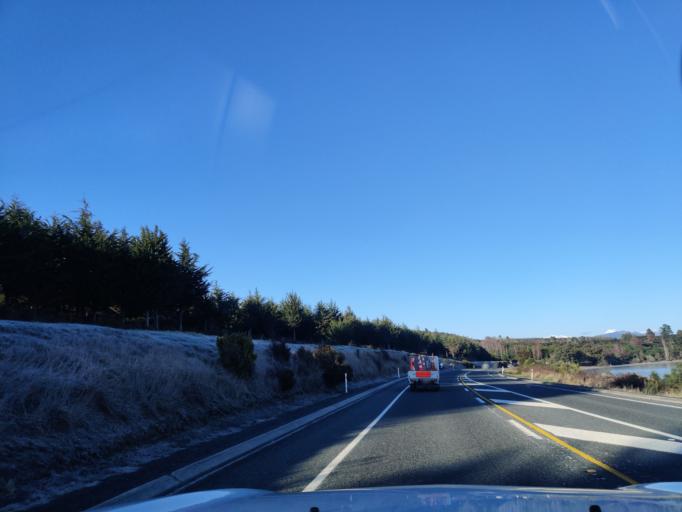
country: NZ
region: Waikato
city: Turangi
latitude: -38.9010
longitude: 175.9440
